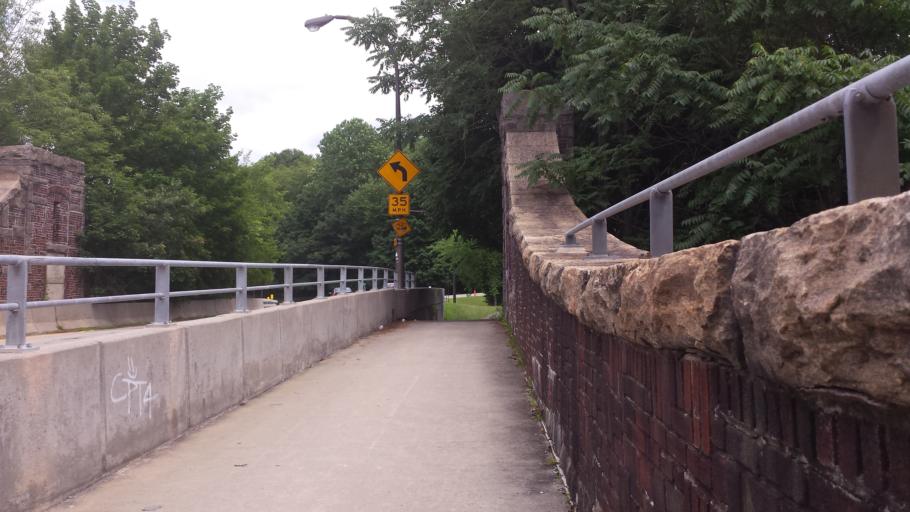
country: US
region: New York
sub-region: Westchester County
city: Valhalla
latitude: 41.0665
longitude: -73.7718
